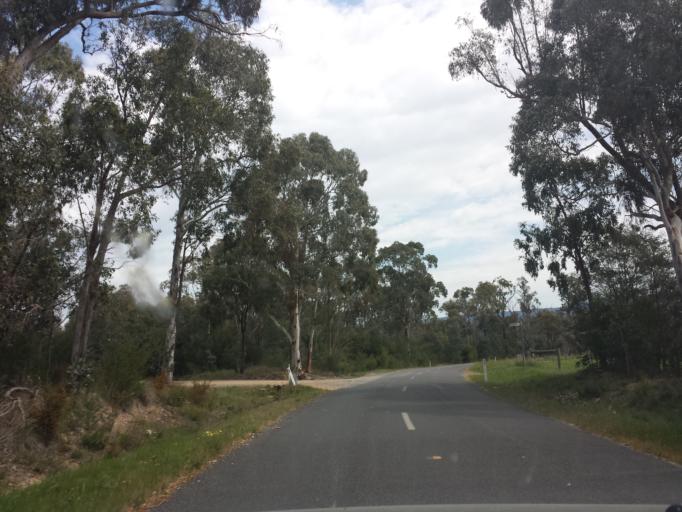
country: AU
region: Victoria
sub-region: Murrindindi
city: Alexandra
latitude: -37.3410
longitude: 145.7315
